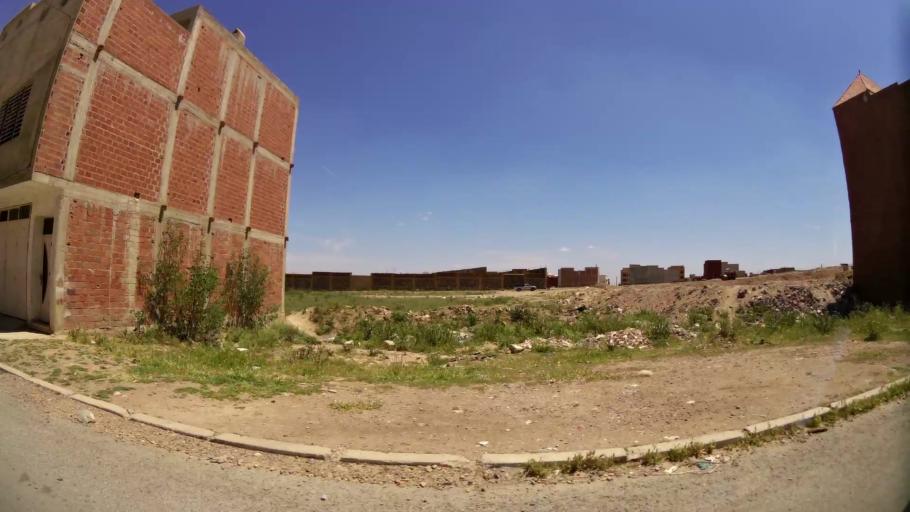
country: MA
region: Oriental
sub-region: Oujda-Angad
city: Oujda
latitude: 34.6572
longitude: -1.9486
